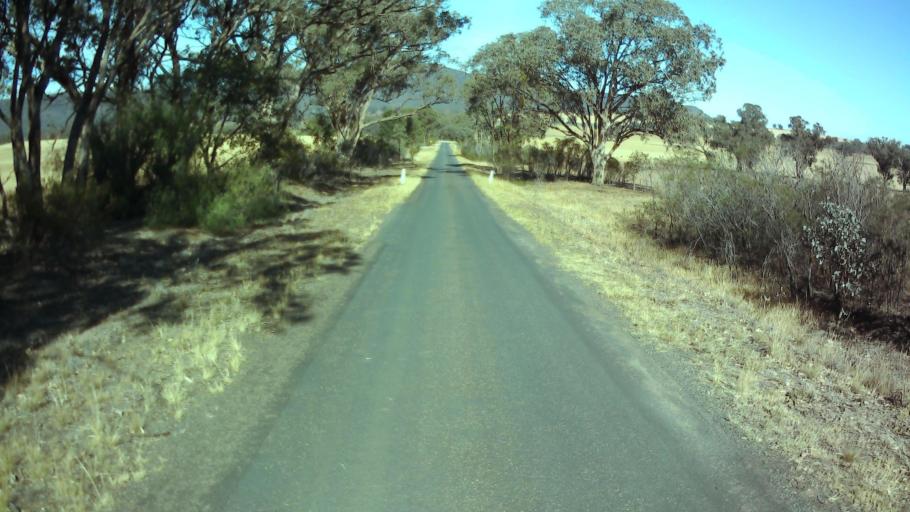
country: AU
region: New South Wales
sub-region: Weddin
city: Grenfell
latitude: -33.9039
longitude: 148.0482
